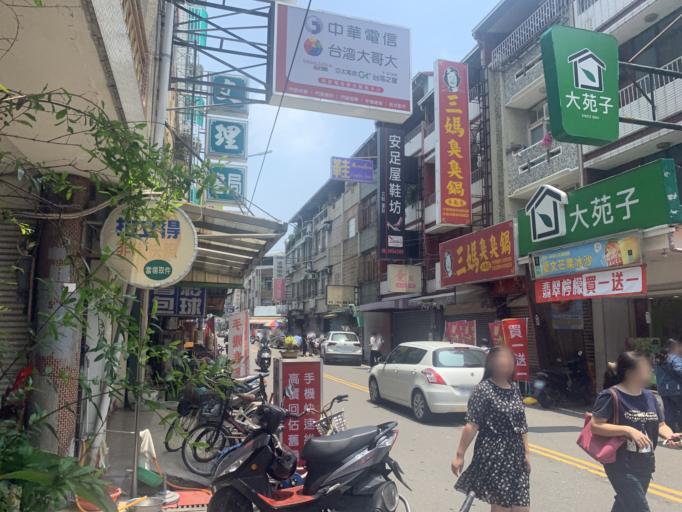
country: TW
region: Taiwan
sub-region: Yunlin
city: Douliu
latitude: 23.6755
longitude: 120.4784
